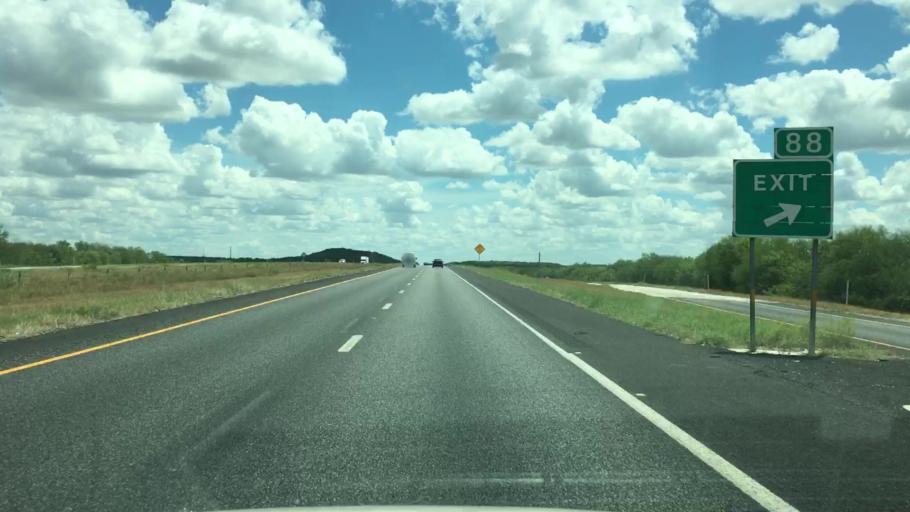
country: US
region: Texas
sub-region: Live Oak County
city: Three Rivers
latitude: 28.7370
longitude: -98.2906
